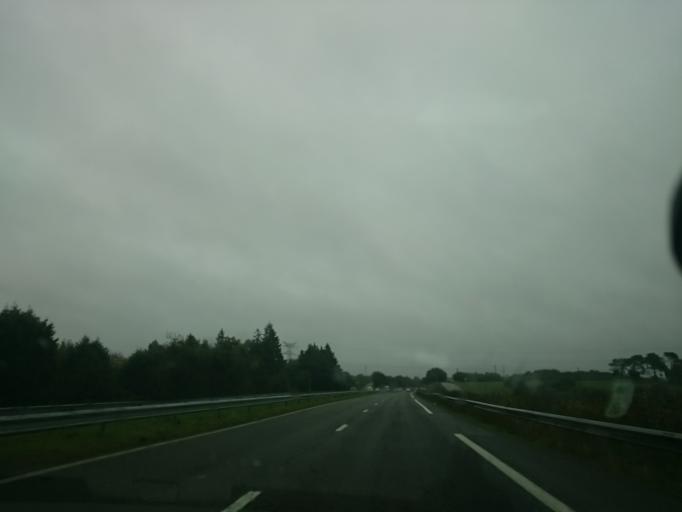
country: FR
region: Brittany
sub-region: Departement du Morbihan
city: Ploeren
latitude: 47.6612
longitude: -2.8319
